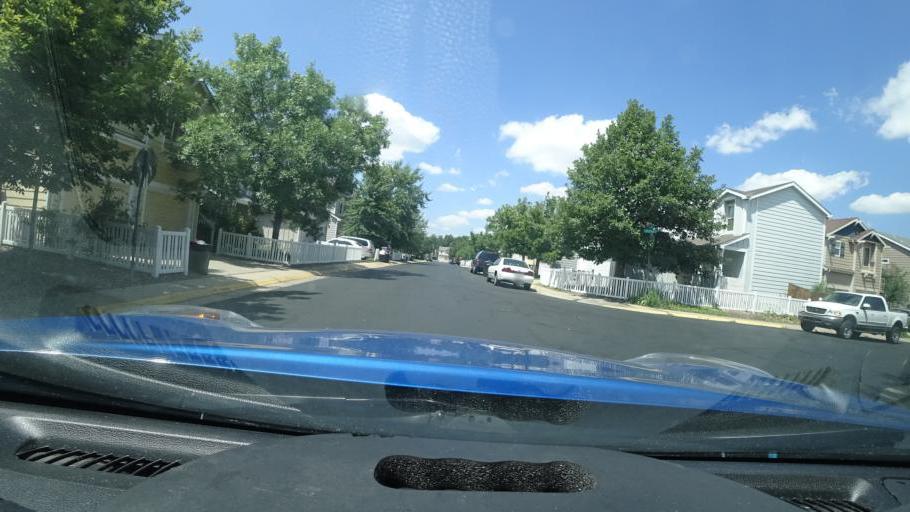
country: US
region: Colorado
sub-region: Arapahoe County
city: Glendale
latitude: 39.6943
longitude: -104.8791
